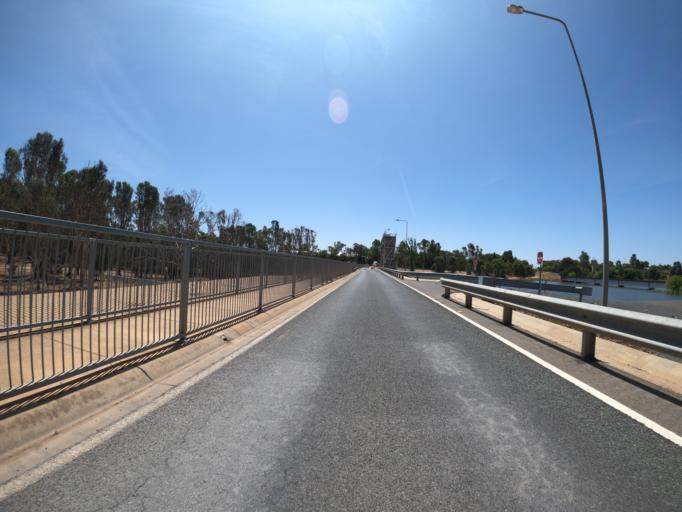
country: AU
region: Victoria
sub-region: Moira
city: Yarrawonga
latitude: -36.0067
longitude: 145.9984
